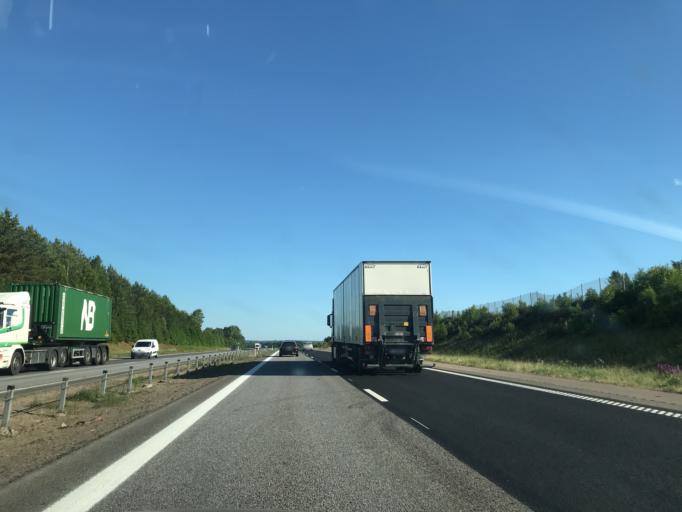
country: SE
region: Halland
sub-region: Halmstads Kommun
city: Aled
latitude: 56.7258
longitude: 12.8819
